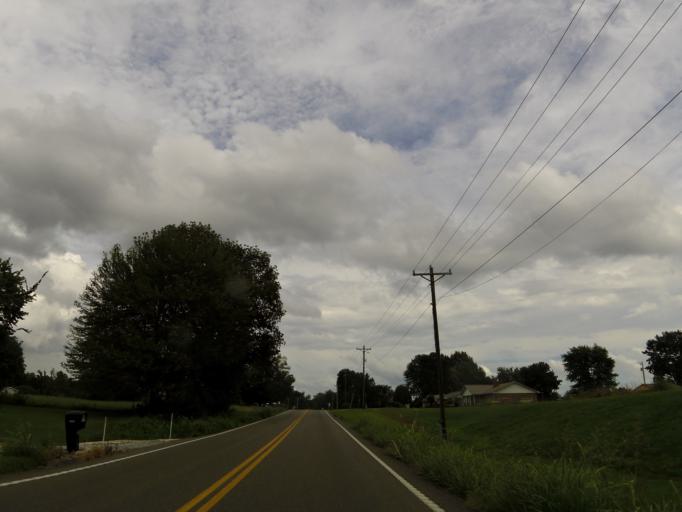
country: US
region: Kentucky
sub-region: Ballard County
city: La Center
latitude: 36.9912
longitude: -88.8917
